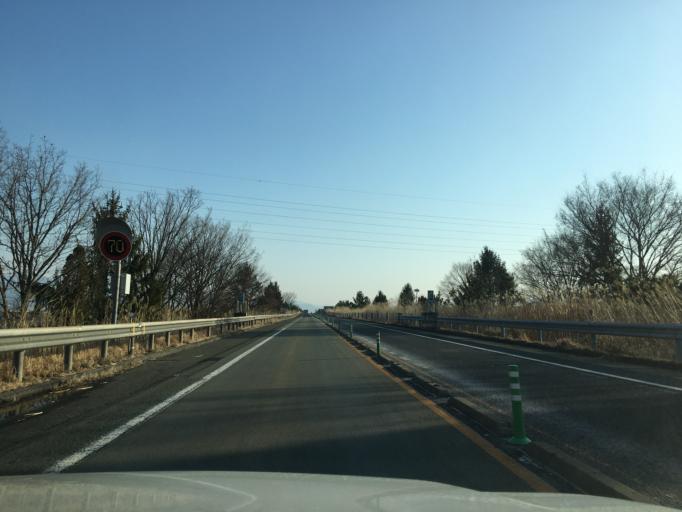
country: JP
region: Yamagata
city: Sagae
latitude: 38.3421
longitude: 140.2972
